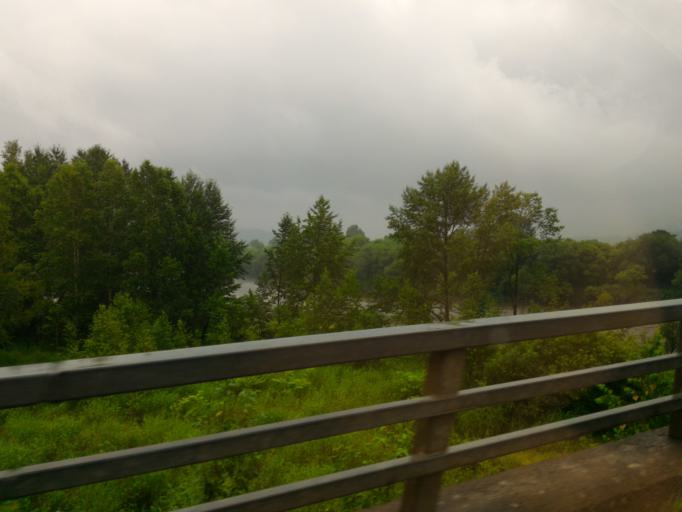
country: JP
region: Hokkaido
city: Nayoro
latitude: 44.5925
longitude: 142.3081
